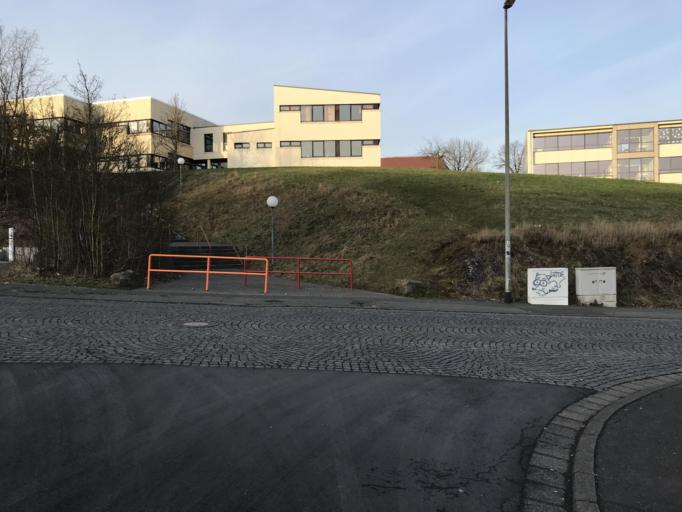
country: DE
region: Hesse
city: Weilburg
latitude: 50.4925
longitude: 8.2612
